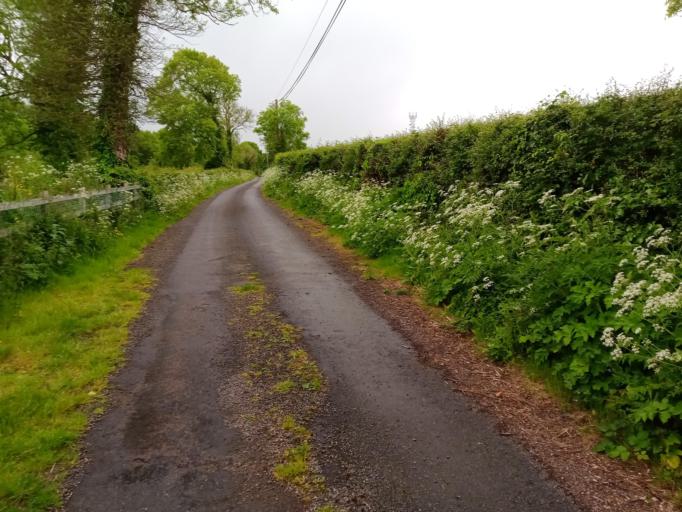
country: IE
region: Leinster
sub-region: Kilkenny
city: Thomastown
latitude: 52.5149
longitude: -7.1342
